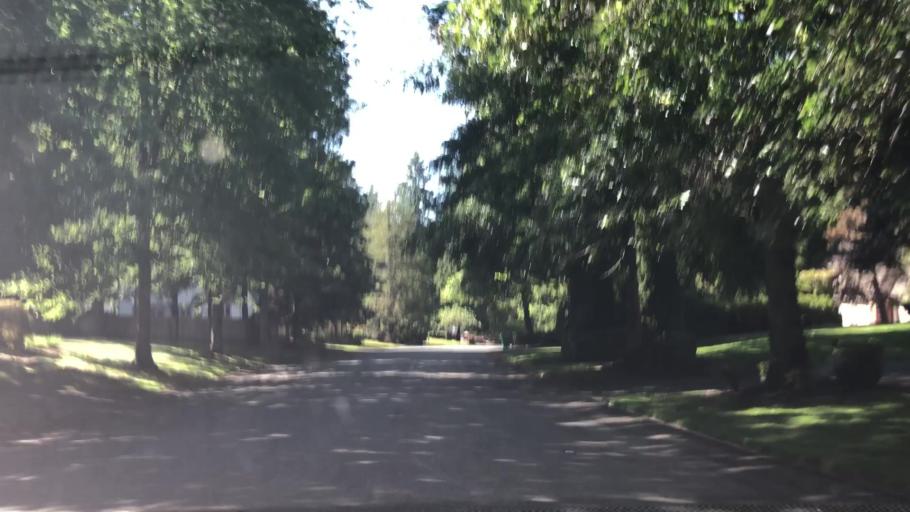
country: US
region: Washington
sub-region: King County
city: Cottage Lake
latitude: 47.7139
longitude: -122.0727
